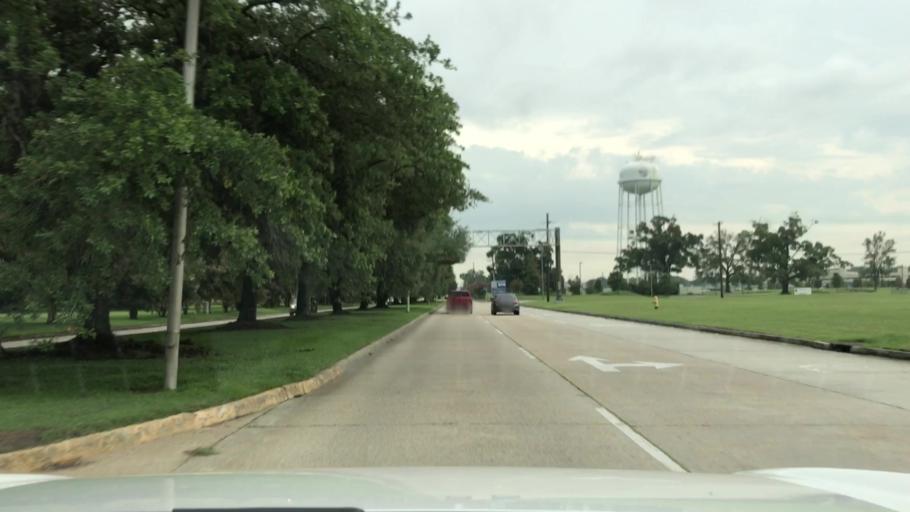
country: US
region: Louisiana
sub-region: East Baton Rouge Parish
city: Brownsfield
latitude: 30.5268
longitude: -91.1610
